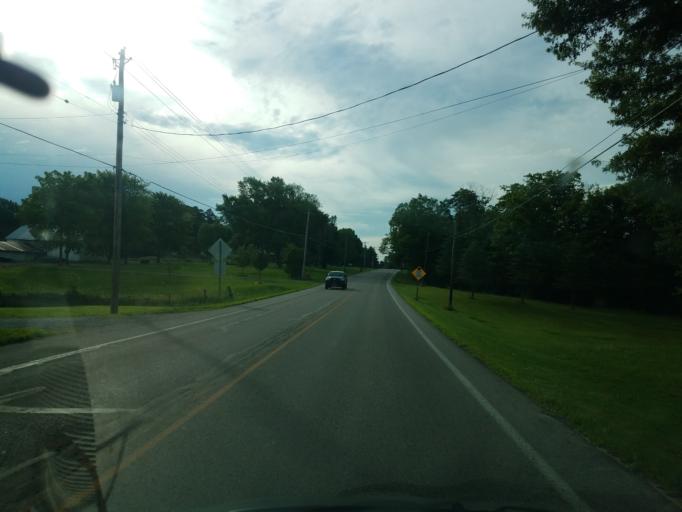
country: US
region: Ohio
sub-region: Ashland County
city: Ashland
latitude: 40.8806
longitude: -82.3438
